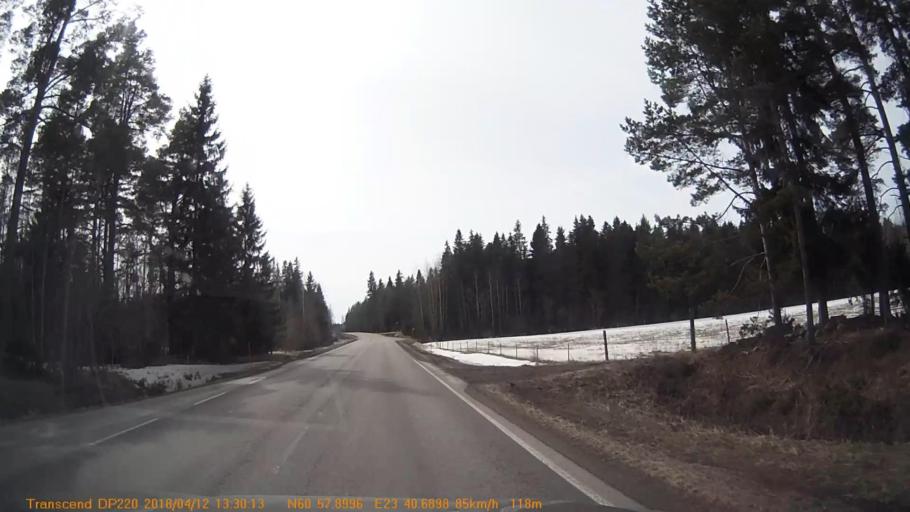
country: FI
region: Haeme
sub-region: Forssa
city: Forssa
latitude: 60.9649
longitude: 23.6781
